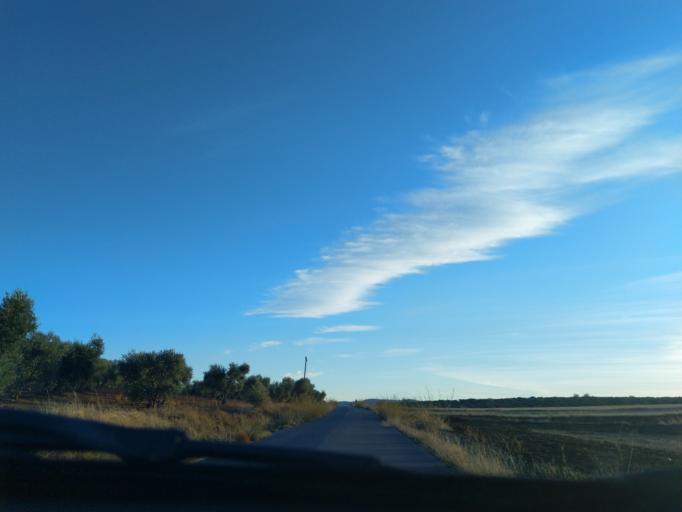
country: ES
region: Extremadura
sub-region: Provincia de Badajoz
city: Valverde de Llerena
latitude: 38.2252
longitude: -5.8224
